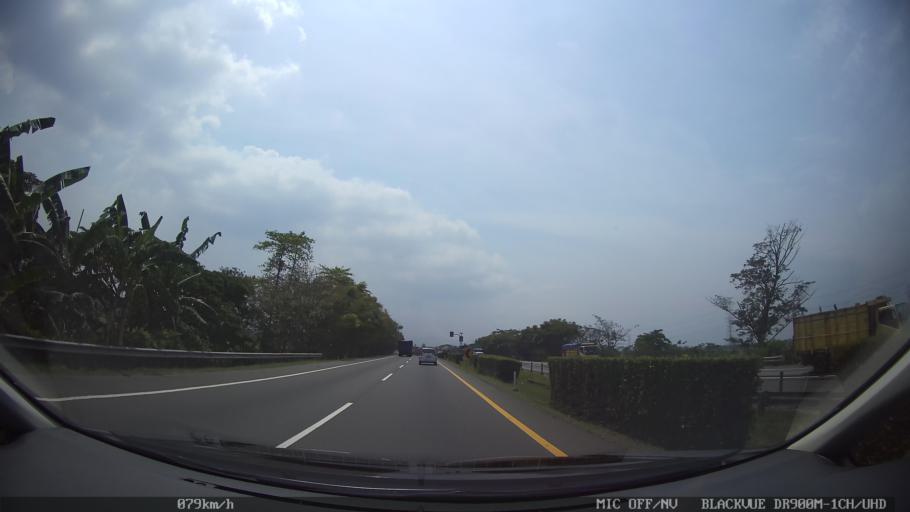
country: ID
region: Banten
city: Serang
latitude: -6.0507
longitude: 106.1165
